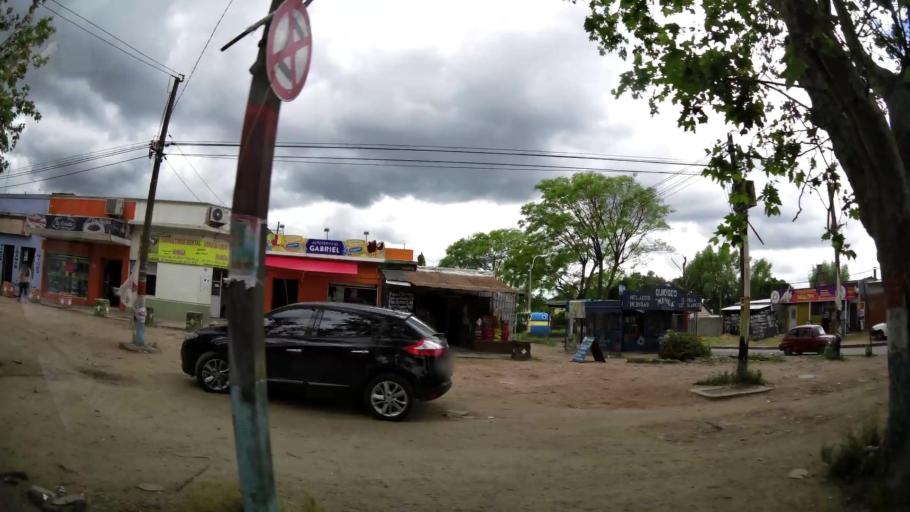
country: UY
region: Canelones
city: Toledo
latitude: -34.8071
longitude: -56.1370
